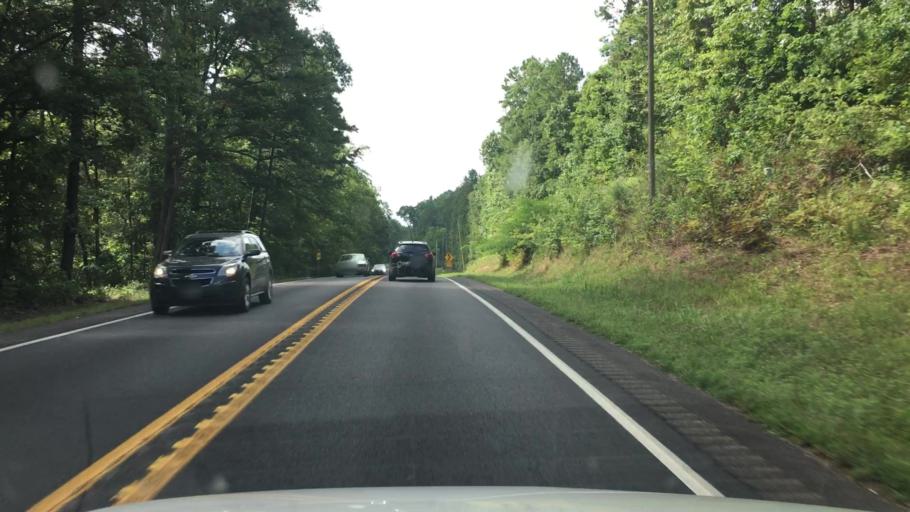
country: US
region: Arkansas
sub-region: Garland County
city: Lake Hamilton
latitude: 34.3470
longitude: -93.1844
